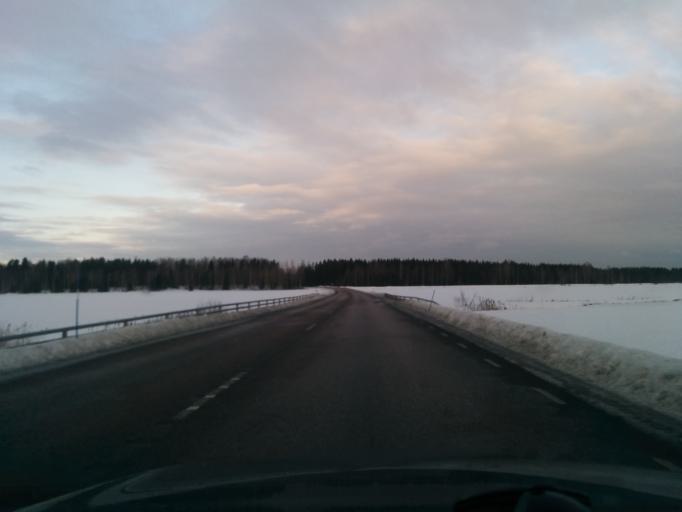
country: SE
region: Uppsala
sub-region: Tierps Kommun
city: Orbyhus
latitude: 60.1791
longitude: 17.6170
